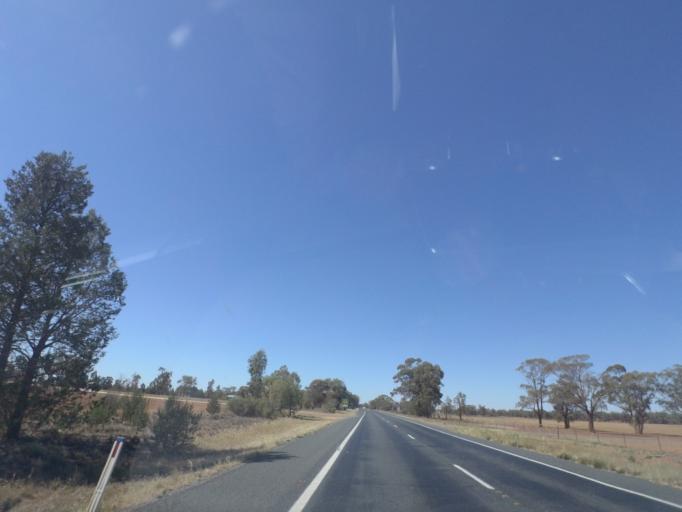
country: AU
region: New South Wales
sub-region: Bland
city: West Wyalong
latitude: -34.1911
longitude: 147.1117
